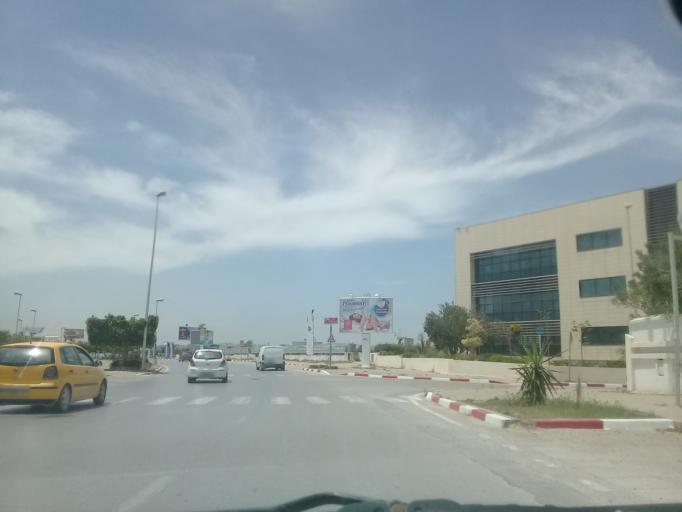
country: TN
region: Ariana
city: Ariana
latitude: 36.8350
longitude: 10.2276
